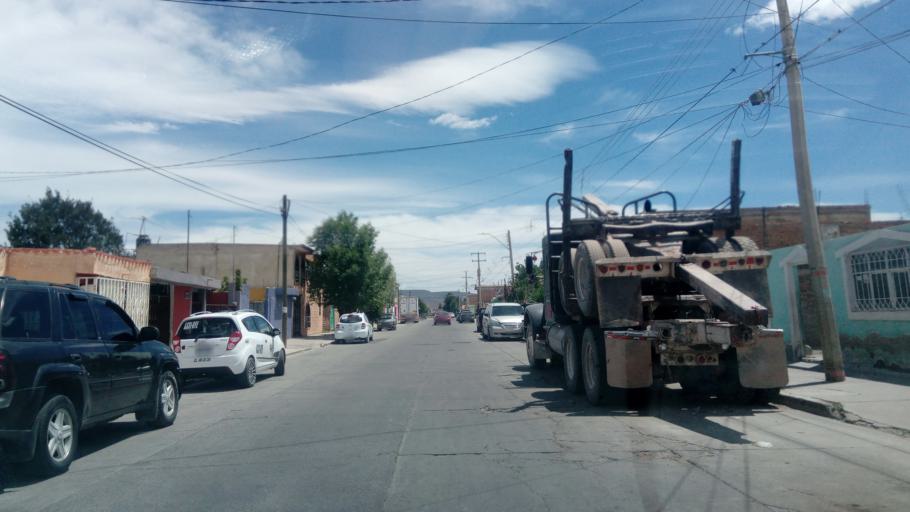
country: MX
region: Durango
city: Victoria de Durango
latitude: 23.9956
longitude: -104.6763
